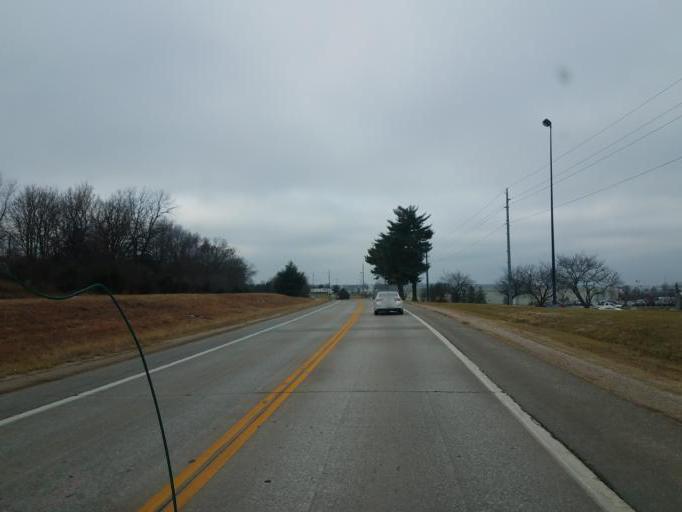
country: US
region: Missouri
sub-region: Greene County
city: Strafford
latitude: 37.2470
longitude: -93.1898
